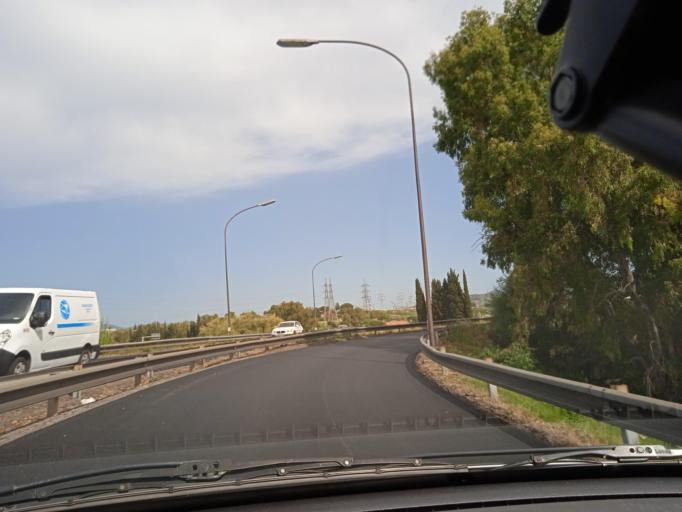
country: IT
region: Sicily
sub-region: Messina
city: San Filippo del Mela
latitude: 38.1934
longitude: 15.2743
